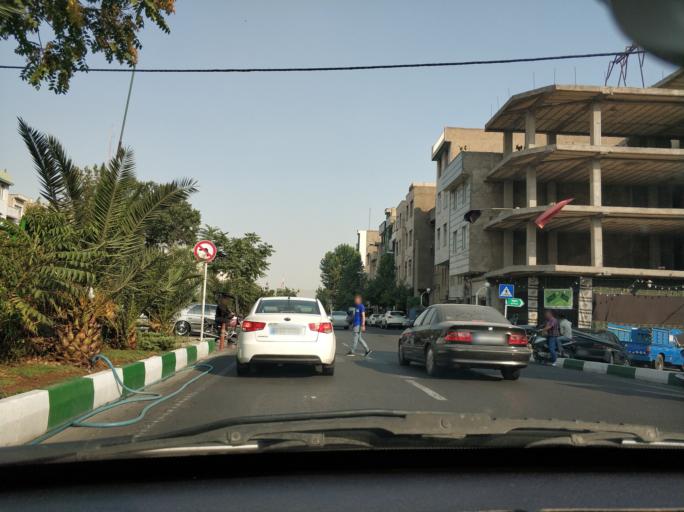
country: IR
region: Tehran
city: Tehran
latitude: 35.7288
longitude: 51.4664
